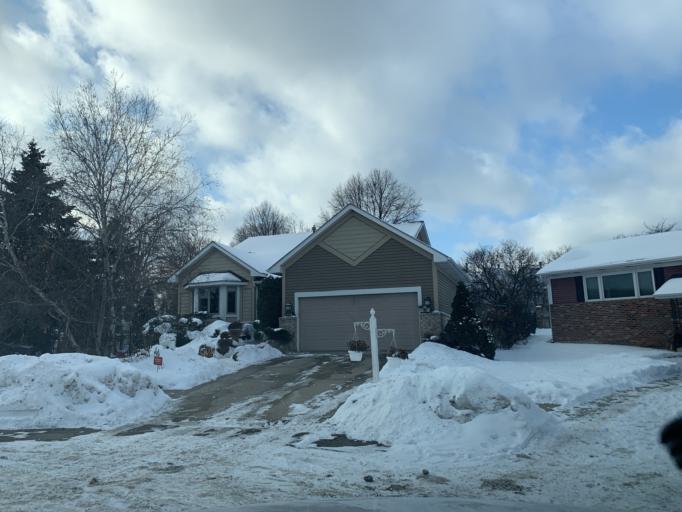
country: US
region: Minnesota
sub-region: Hennepin County
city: Minneapolis
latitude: 44.9925
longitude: -93.2872
